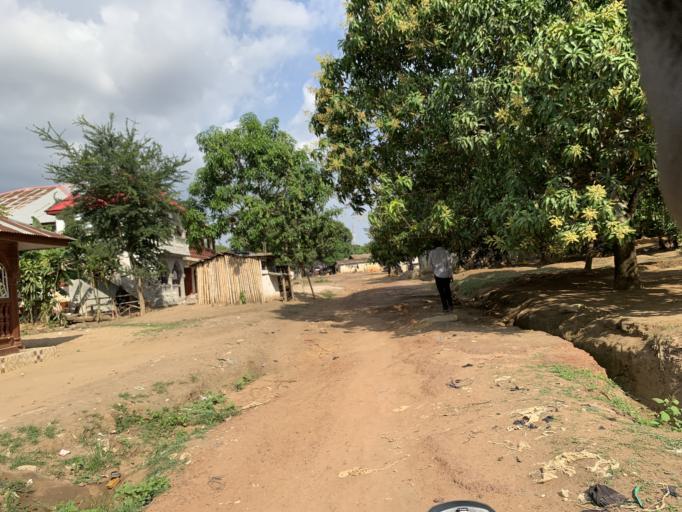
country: SL
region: Western Area
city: Waterloo
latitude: 8.3396
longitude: -13.0448
